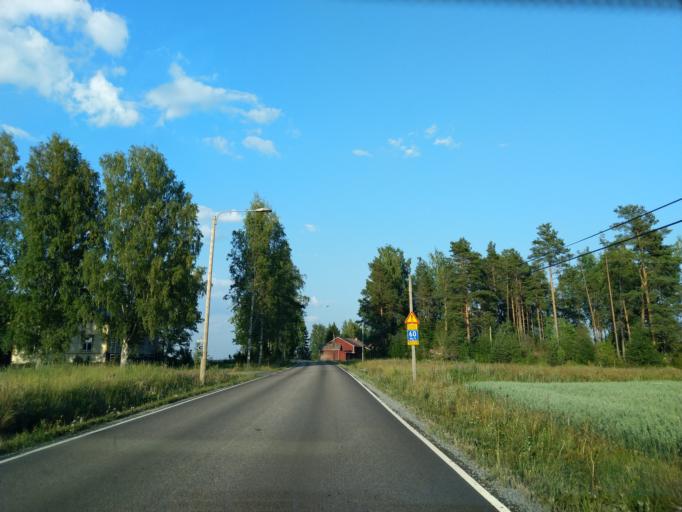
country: FI
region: Satakunta
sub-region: Pohjois-Satakunta
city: Kankaanpaeae
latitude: 61.8217
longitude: 22.2706
